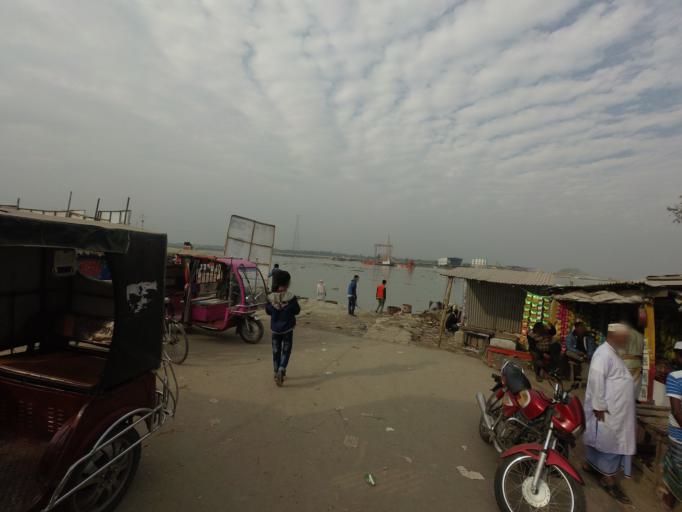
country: BD
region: Barisal
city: Nalchiti
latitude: 22.4634
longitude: 90.3415
